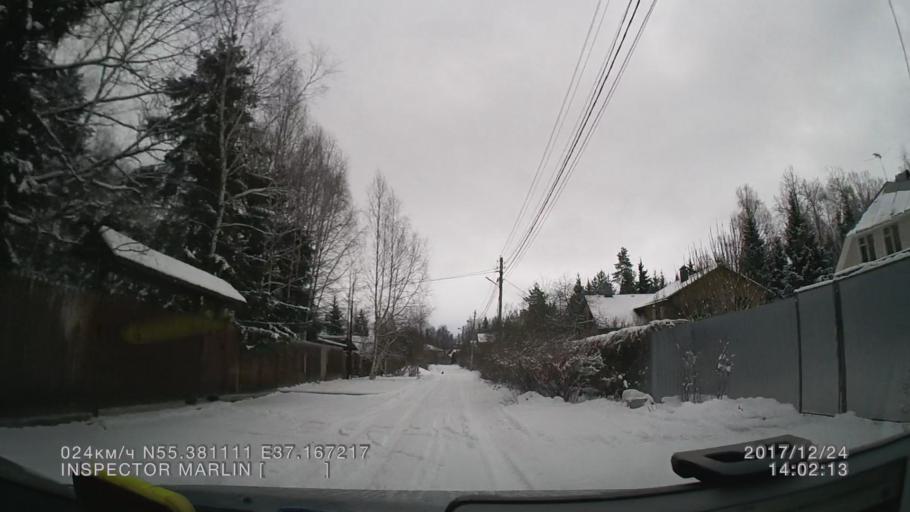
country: RU
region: Moskovskaya
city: Troitsk
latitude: 55.3812
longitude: 37.1671
